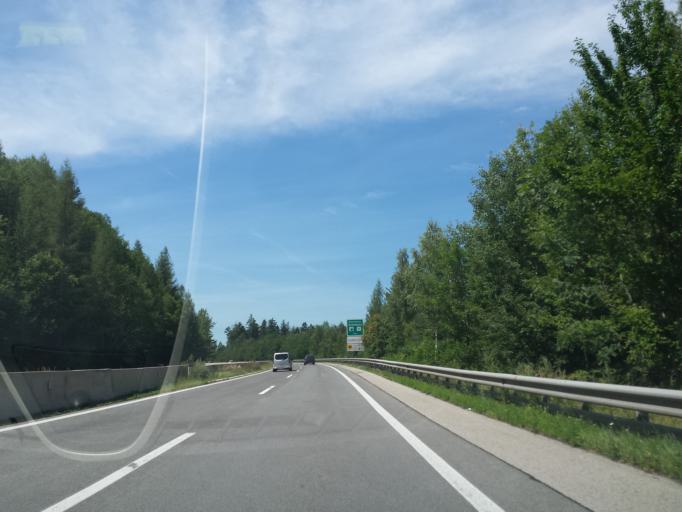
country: AT
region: Lower Austria
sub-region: Politischer Bezirk Neunkirchen
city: Raach am Hochgebirge
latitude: 47.6554
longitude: 15.9103
